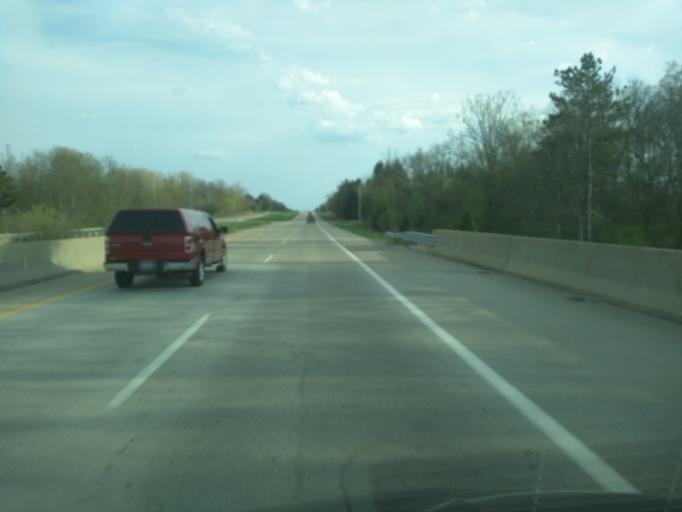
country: US
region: Michigan
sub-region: Eaton County
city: Dimondale
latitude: 42.6312
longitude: -84.6231
